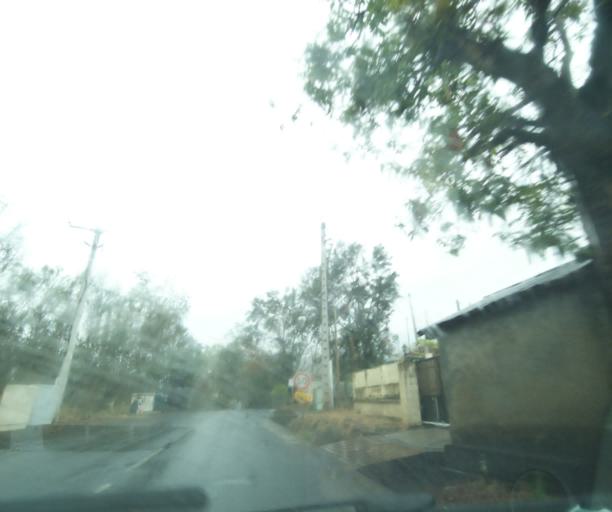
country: RE
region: Reunion
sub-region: Reunion
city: Saint-Paul
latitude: -21.0183
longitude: 55.3021
